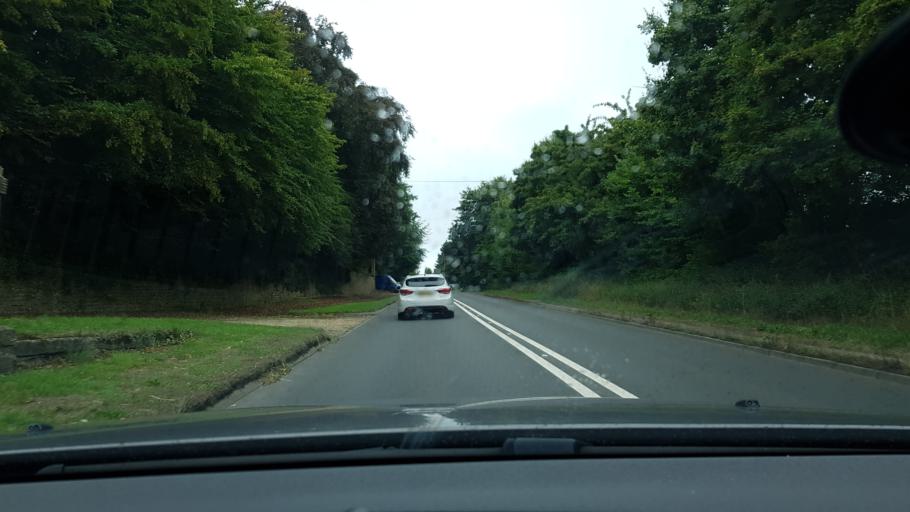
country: GB
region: England
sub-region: Wiltshire
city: Bremhill
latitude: 51.4379
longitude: -2.0355
